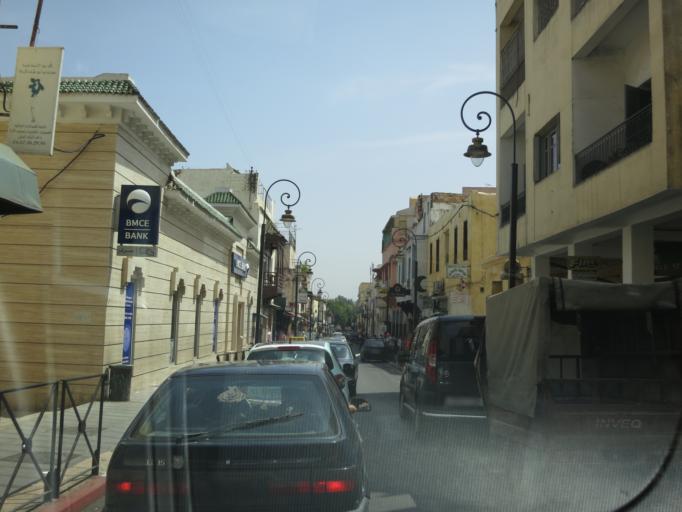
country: MA
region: Meknes-Tafilalet
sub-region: Meknes
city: Meknes
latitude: 33.8945
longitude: -5.5609
